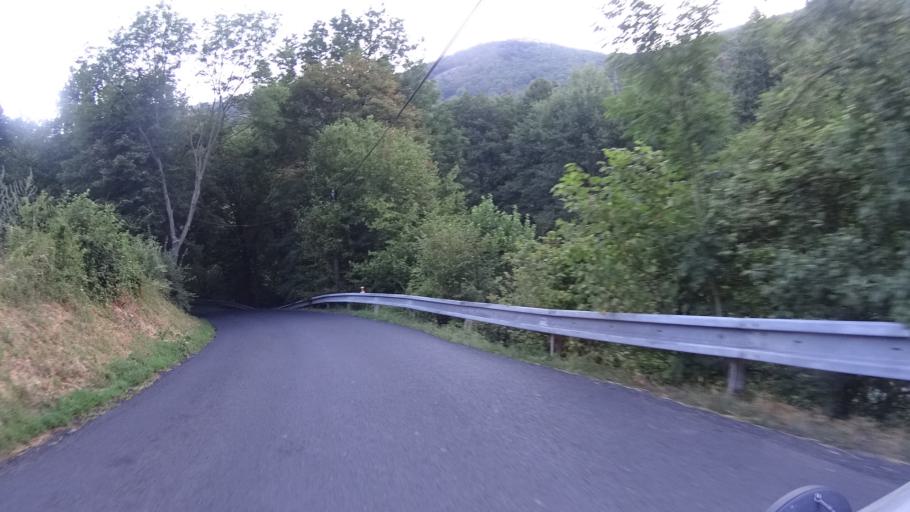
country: CZ
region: Ustecky
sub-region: Okres Litomerice
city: Litomerice
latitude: 50.5865
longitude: 14.0782
